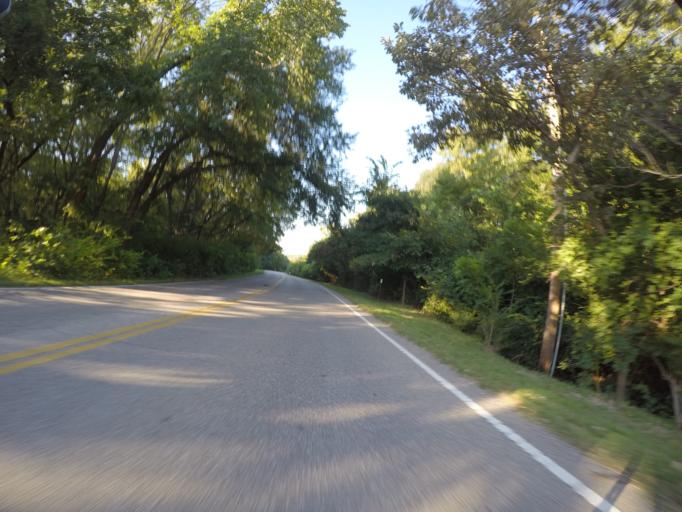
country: US
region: Kansas
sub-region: Riley County
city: Manhattan
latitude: 39.1634
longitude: -96.6045
